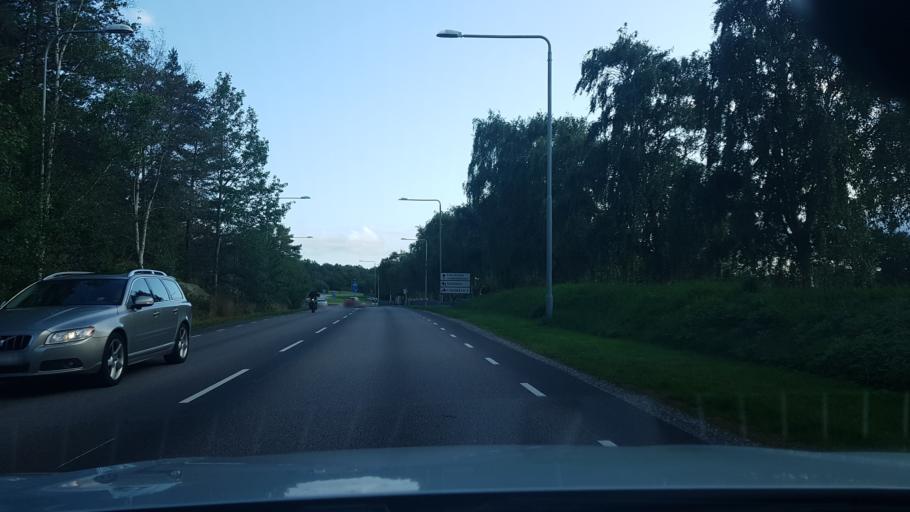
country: SE
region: Vaestra Goetaland
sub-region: Goteborg
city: Majorna
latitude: 57.6497
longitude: 11.8676
